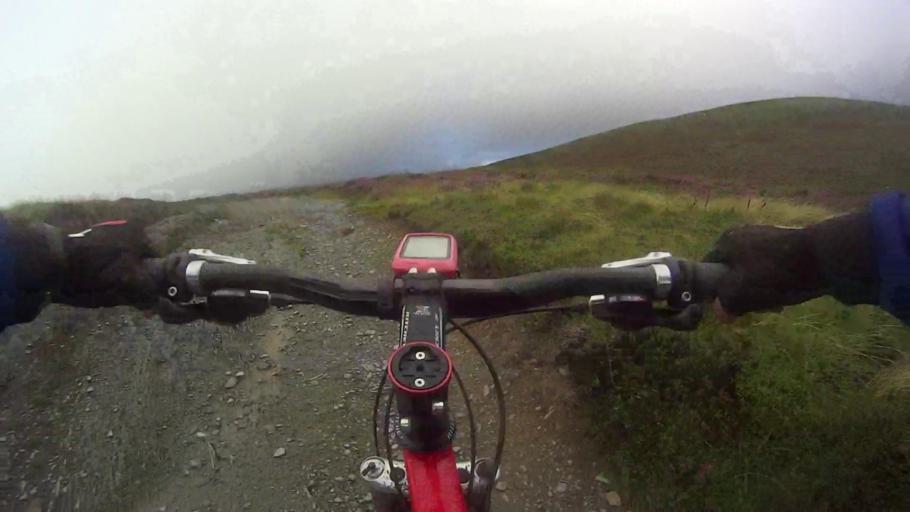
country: GB
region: Wales
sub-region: County of Ceredigion
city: Bow Street
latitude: 52.4304
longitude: -3.8943
